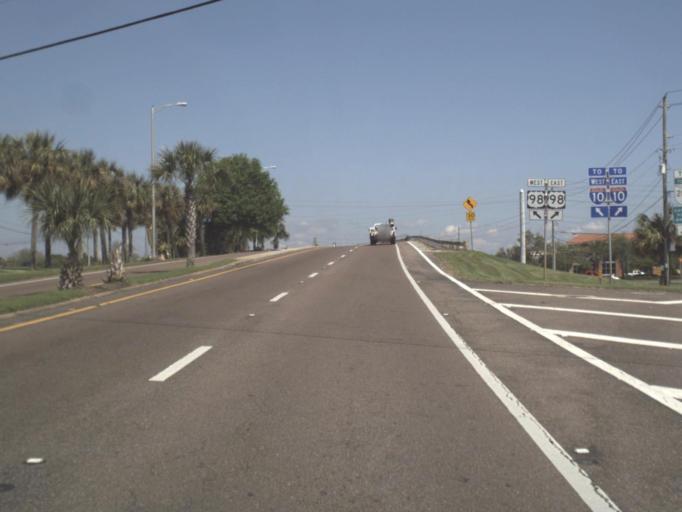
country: US
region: Florida
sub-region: Santa Rosa County
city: Gulf Breeze
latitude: 30.3564
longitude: -87.1591
